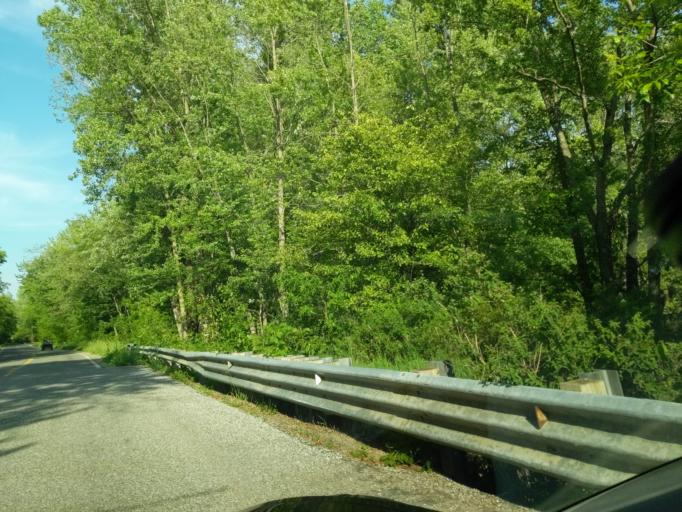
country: US
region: Michigan
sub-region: Barry County
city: Nashville
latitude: 42.6244
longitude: -85.1467
